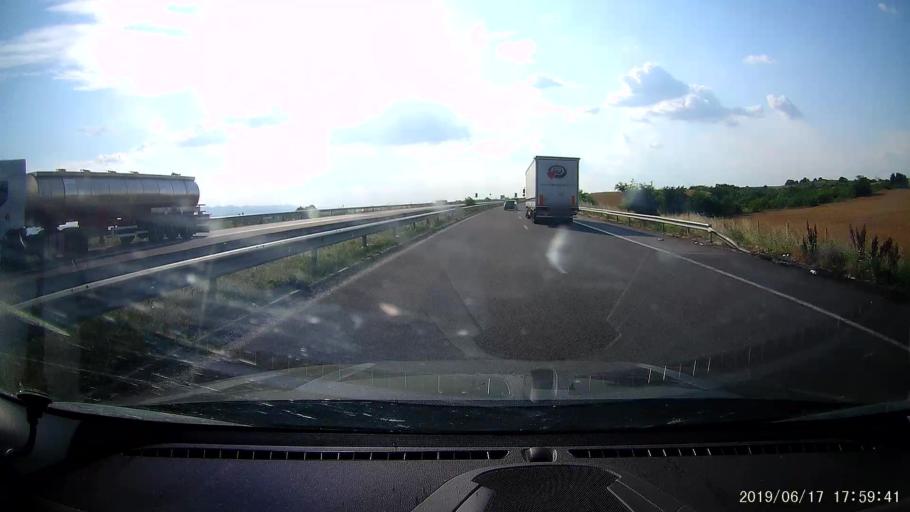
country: BG
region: Khaskovo
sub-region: Obshtina Svilengrad
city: Svilengrad
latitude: 41.7258
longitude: 26.2918
